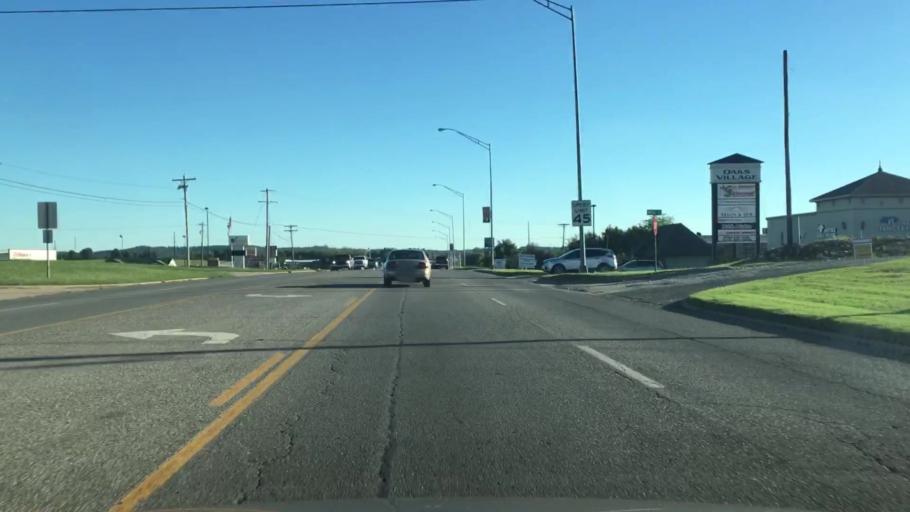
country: US
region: Oklahoma
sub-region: Cherokee County
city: Park Hill
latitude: 35.8820
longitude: -94.9764
